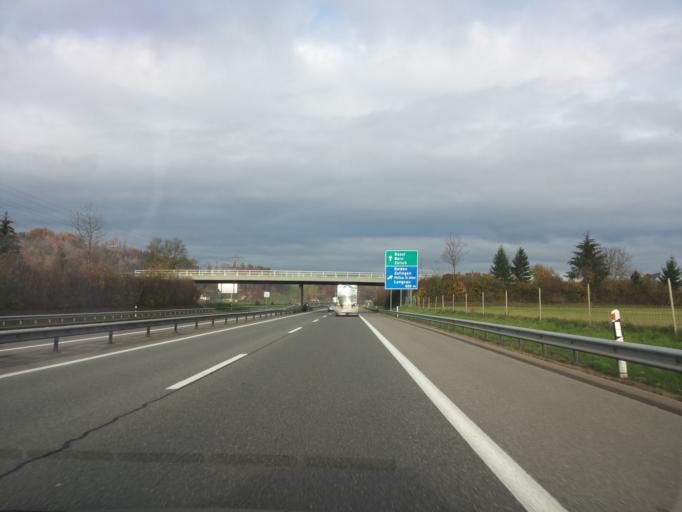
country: CH
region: Lucerne
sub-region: Willisau District
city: Reiden
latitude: 47.2358
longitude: 7.9650
